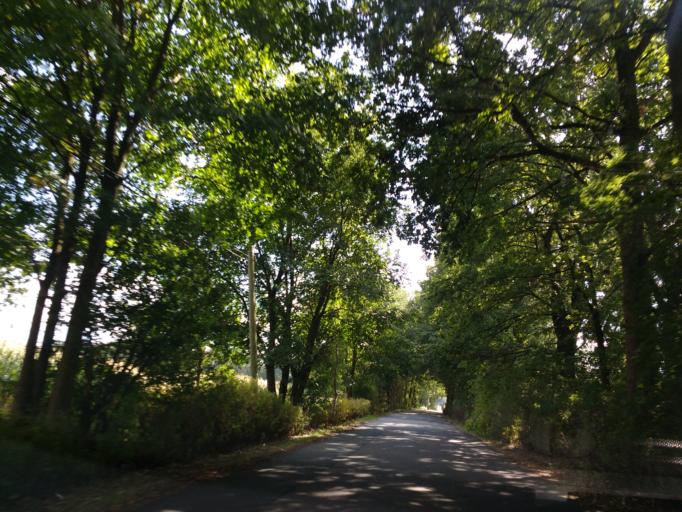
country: DE
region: North Rhine-Westphalia
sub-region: Regierungsbezirk Detmold
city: Hovelhof
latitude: 51.8067
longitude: 8.6797
